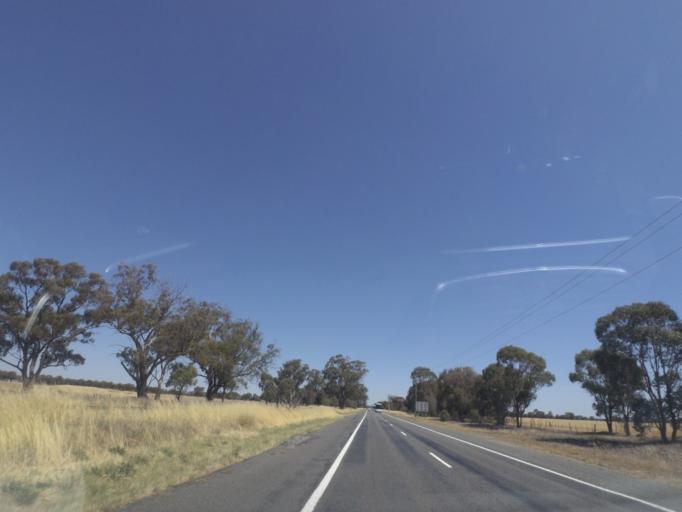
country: AU
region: Victoria
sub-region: Greater Shepparton
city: Shepparton
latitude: -36.2062
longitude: 145.4319
